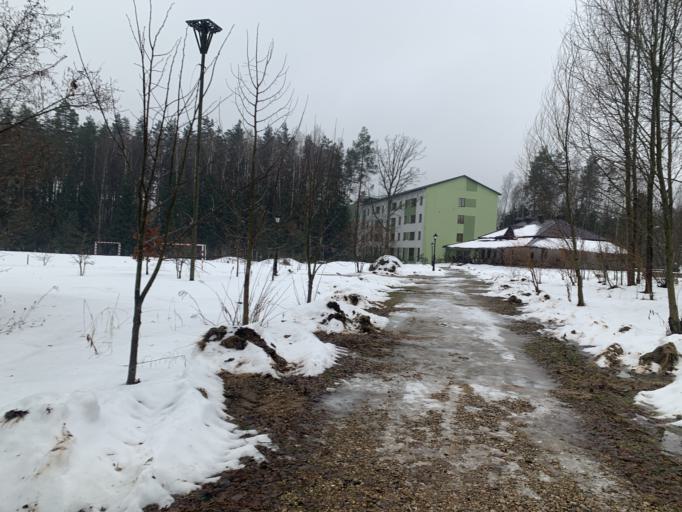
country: BY
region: Minsk
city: Slabada
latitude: 53.9499
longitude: 27.9823
